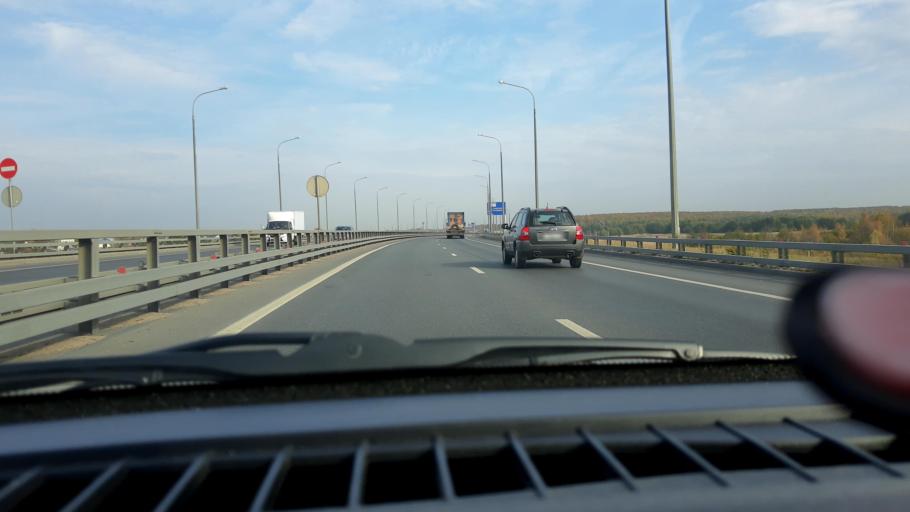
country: RU
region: Nizjnij Novgorod
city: Neklyudovo
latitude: 56.3914
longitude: 43.9779
